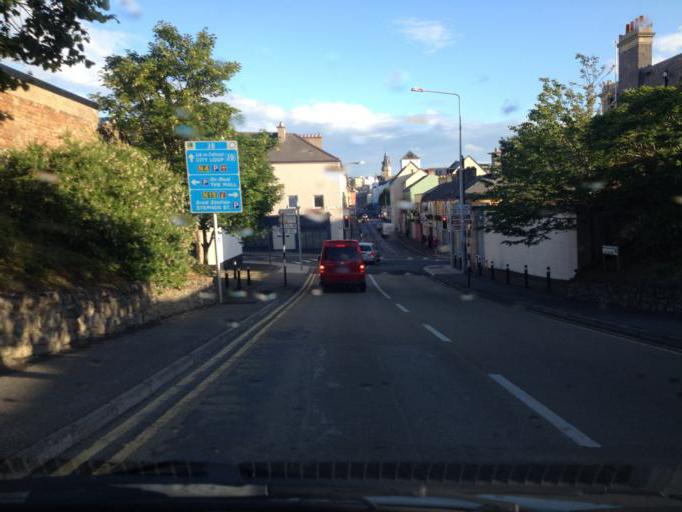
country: IE
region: Connaught
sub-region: Sligo
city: Sligo
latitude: 54.2730
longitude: -8.4714
